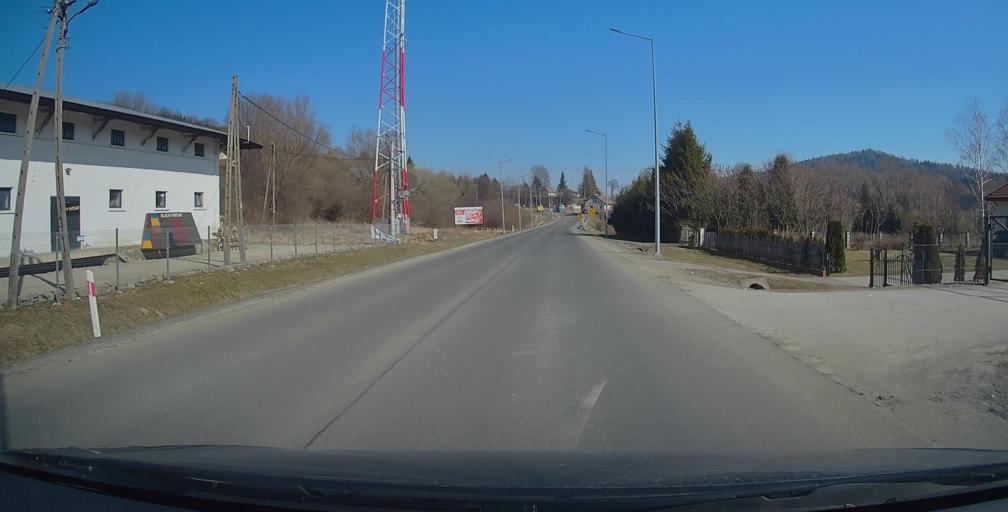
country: PL
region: Subcarpathian Voivodeship
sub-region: Powiat bieszczadzki
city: Ustrzyki Dolne
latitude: 49.4780
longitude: 22.6702
